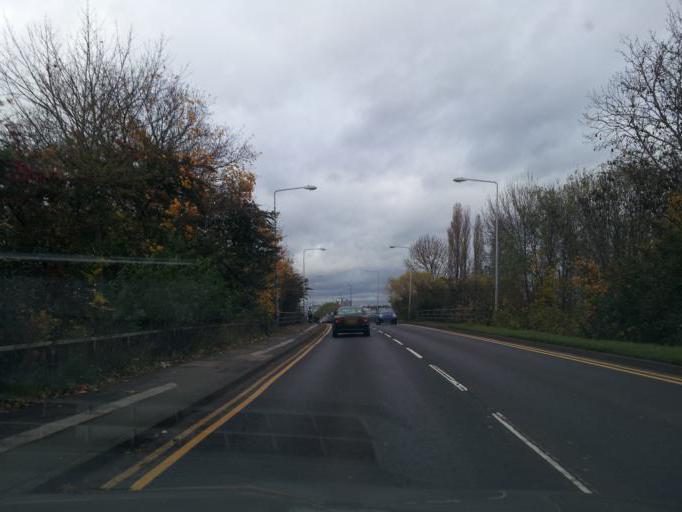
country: GB
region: England
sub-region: Nottinghamshire
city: West Bridgford
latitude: 52.9412
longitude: -1.1303
